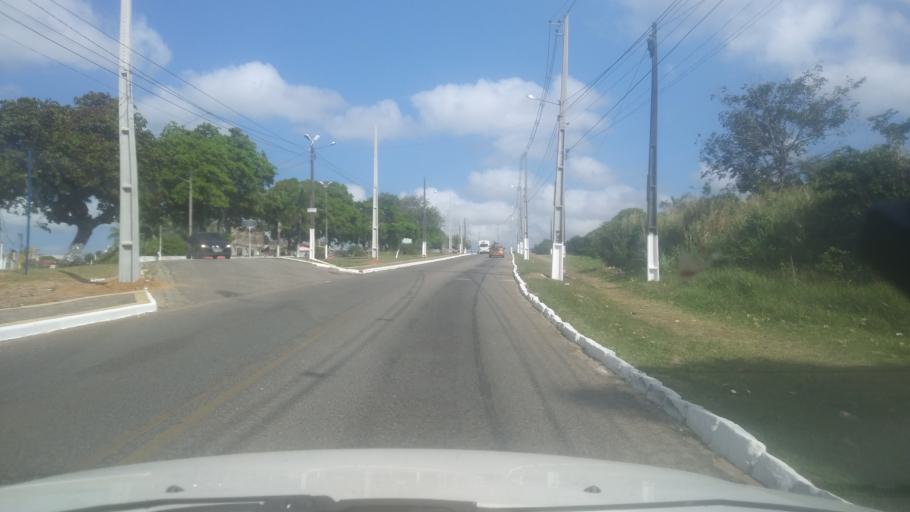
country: BR
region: Rio Grande do Norte
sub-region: Extremoz
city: Extremoz
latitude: -5.7043
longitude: -35.2861
